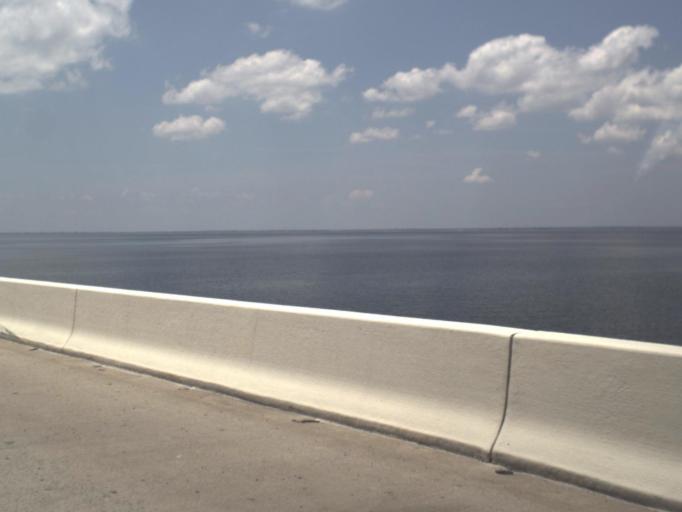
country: US
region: Florida
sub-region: Hillsborough County
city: Town 'n' Country
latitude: 27.9333
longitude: -82.5732
